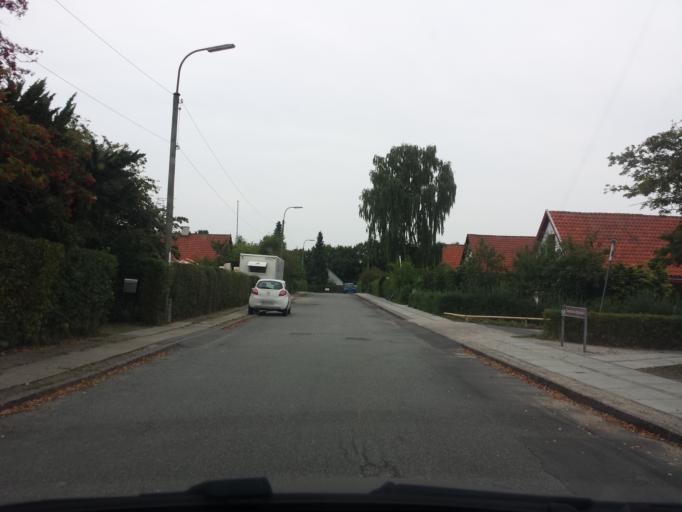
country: DK
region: Capital Region
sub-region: Herlev Kommune
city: Herlev
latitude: 55.7128
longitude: 12.4041
